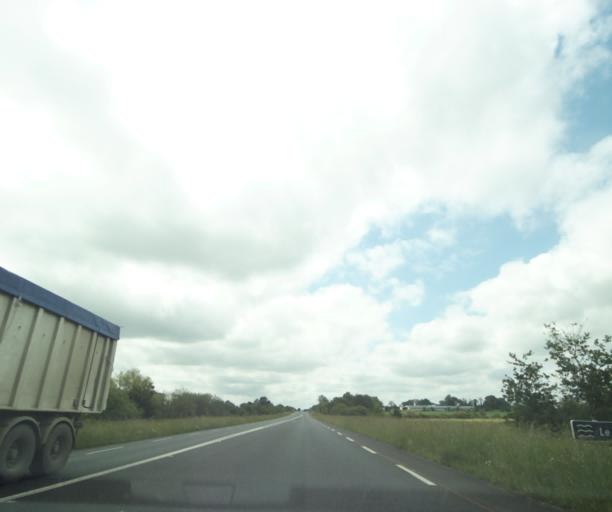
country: FR
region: Poitou-Charentes
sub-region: Departement des Deux-Sevres
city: Airvault
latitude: 46.7875
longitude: -0.2156
